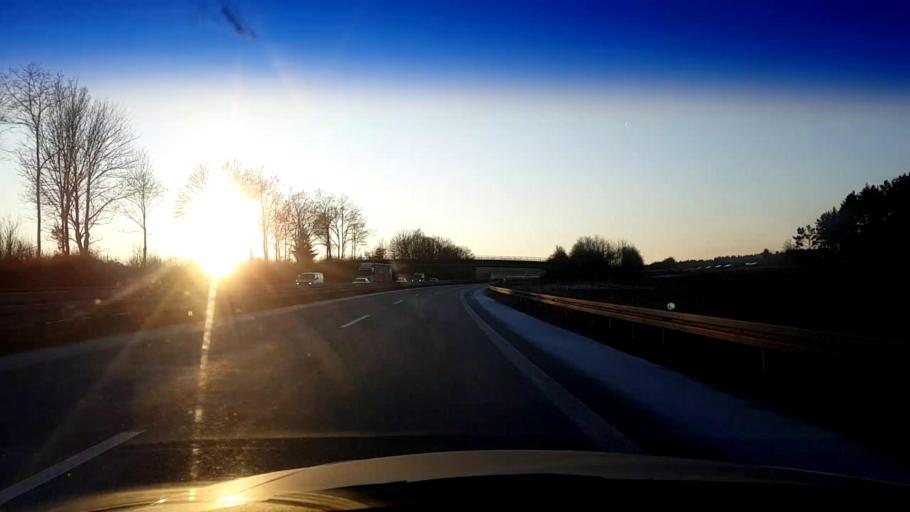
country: DE
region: Bavaria
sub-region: Upper Franconia
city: Wonsees
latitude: 50.0059
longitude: 11.2931
